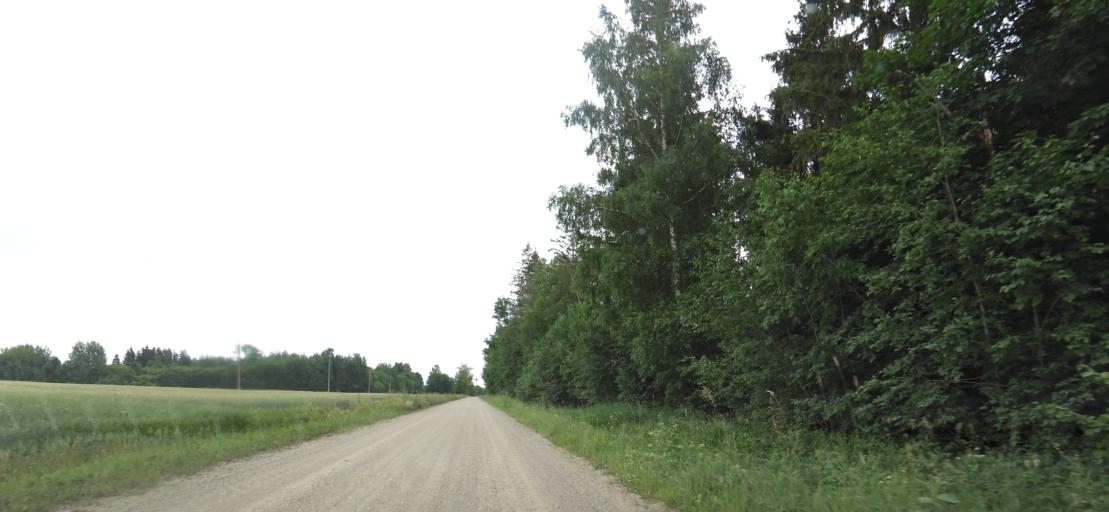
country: LT
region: Panevezys
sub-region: Birzai
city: Birzai
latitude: 56.2979
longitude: 24.9727
